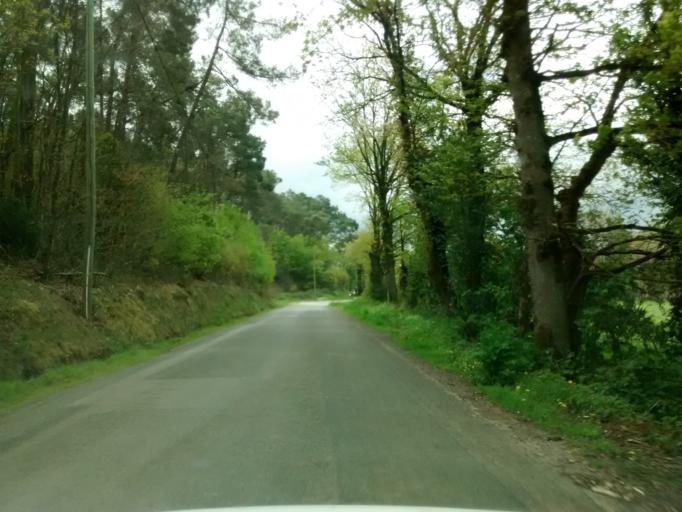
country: FR
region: Brittany
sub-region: Departement du Morbihan
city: Ruffiac
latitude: 47.7737
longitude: -2.3137
